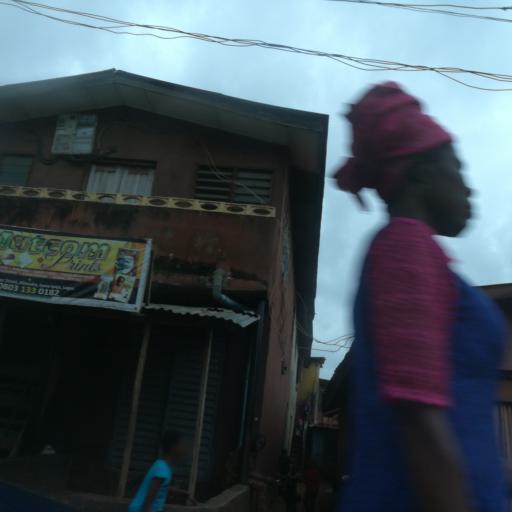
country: NG
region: Lagos
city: Agege
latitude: 6.6108
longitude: 3.2967
